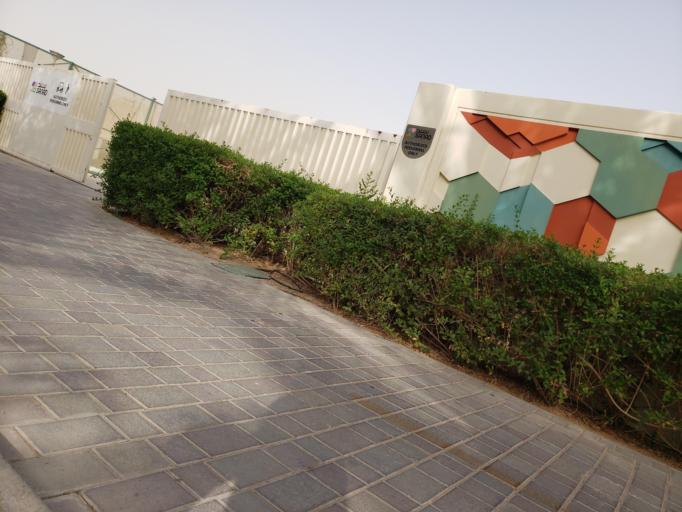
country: AE
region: Dubai
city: Dubai
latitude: 25.0281
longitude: 55.2773
